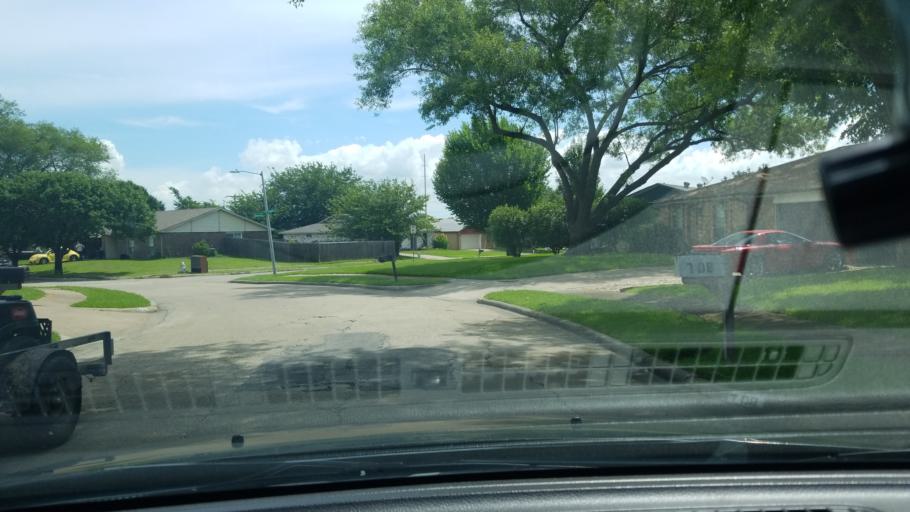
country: US
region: Texas
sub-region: Dallas County
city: Mesquite
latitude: 32.7589
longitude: -96.5767
